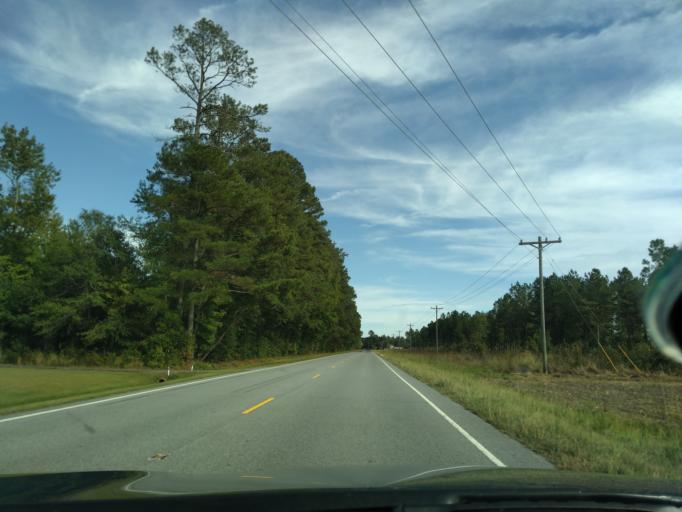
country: US
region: North Carolina
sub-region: Beaufort County
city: River Road
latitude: 35.5219
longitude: -76.8314
